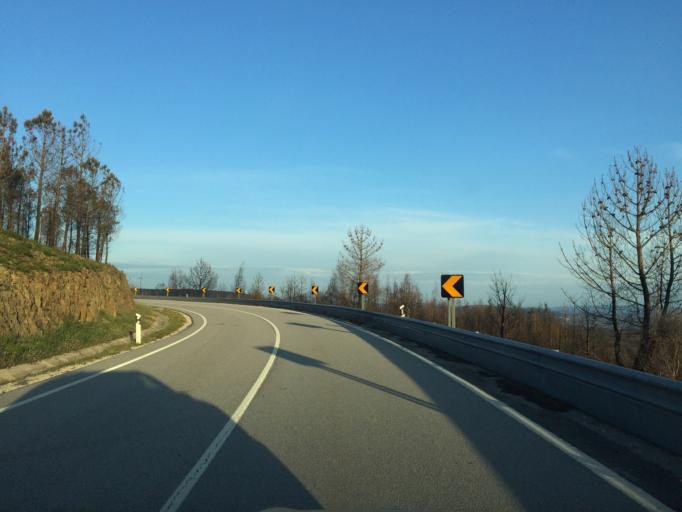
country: PT
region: Coimbra
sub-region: Gois
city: Gois
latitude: 40.1097
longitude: -8.0273
